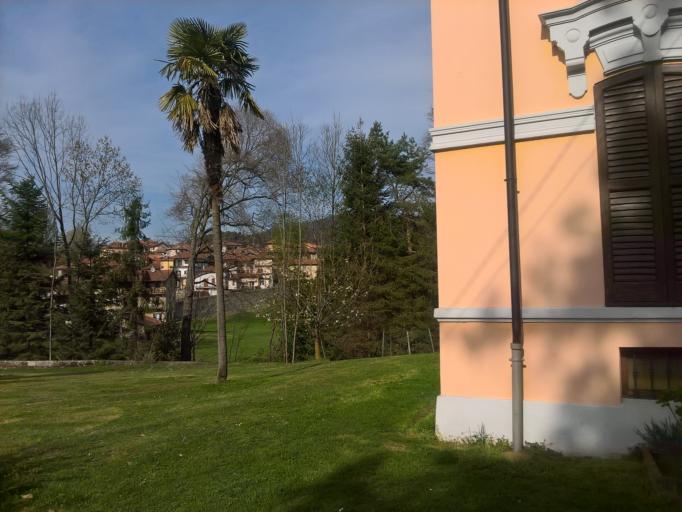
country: IT
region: Piedmont
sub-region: Provincia di Novara
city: Bolzano Novarese
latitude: 45.7607
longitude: 8.4419
